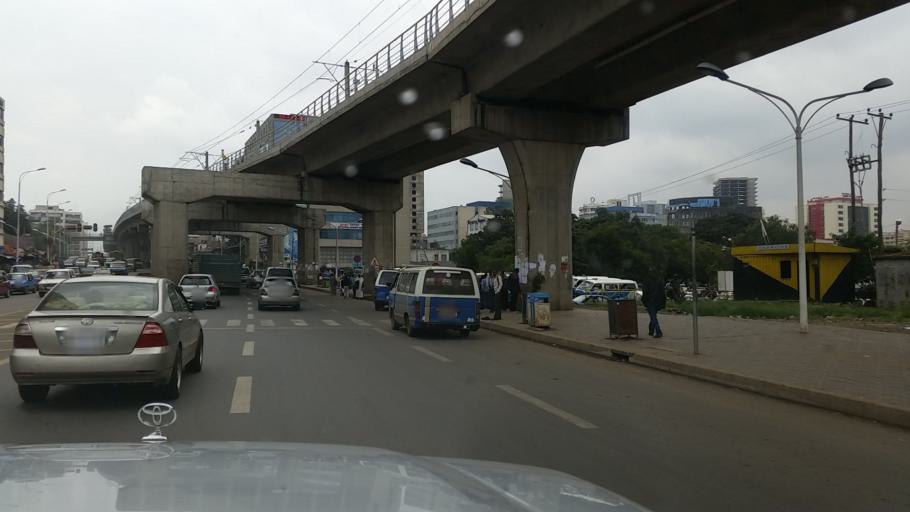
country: ET
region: Adis Abeba
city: Addis Ababa
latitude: 9.0120
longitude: 38.7567
